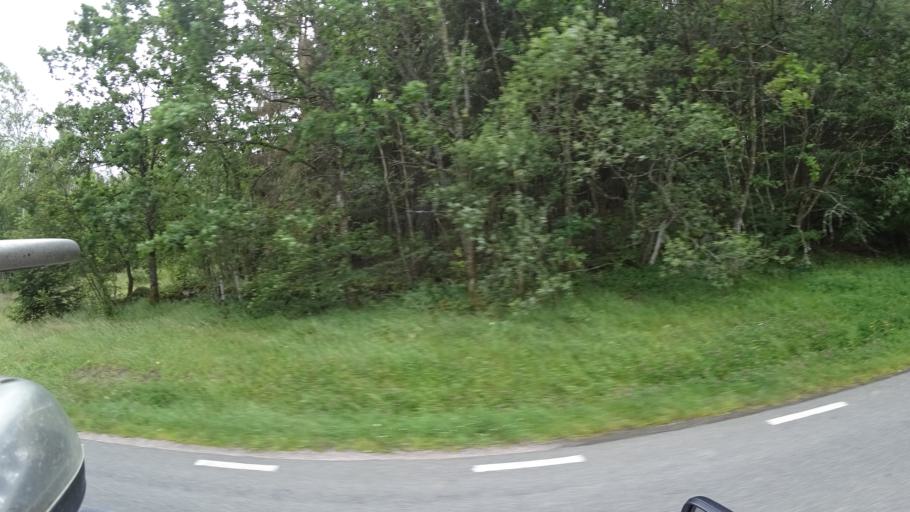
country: SE
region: Skane
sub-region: Kristianstads Kommun
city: Degeberga
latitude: 55.7317
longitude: 13.9499
